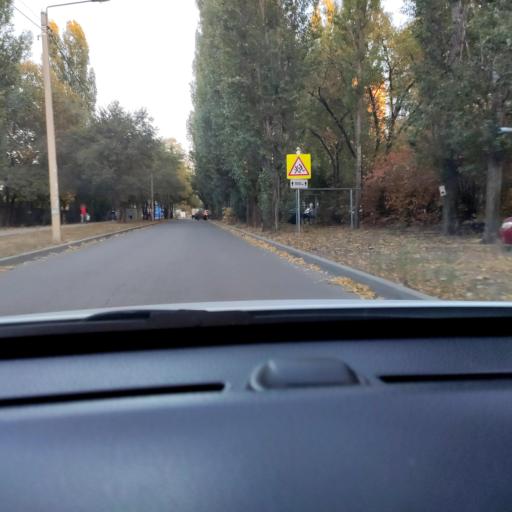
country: RU
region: Voronezj
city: Voronezh
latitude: 51.7204
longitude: 39.2668
